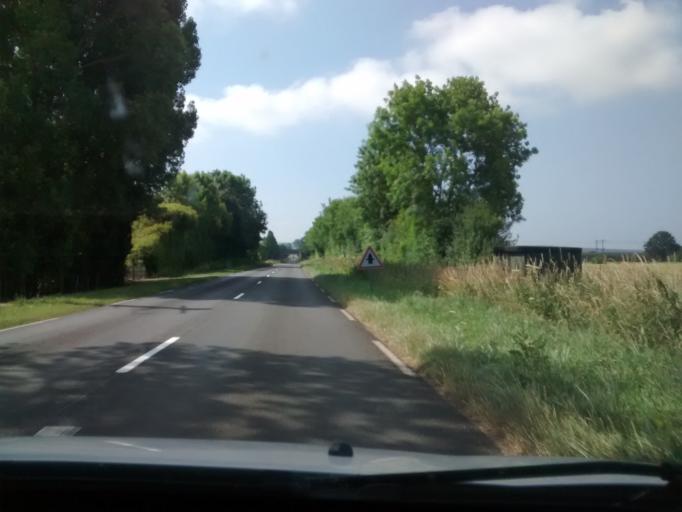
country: FR
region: Pays de la Loire
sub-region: Departement de la Sarthe
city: Vibraye
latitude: 48.0860
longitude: 0.7244
